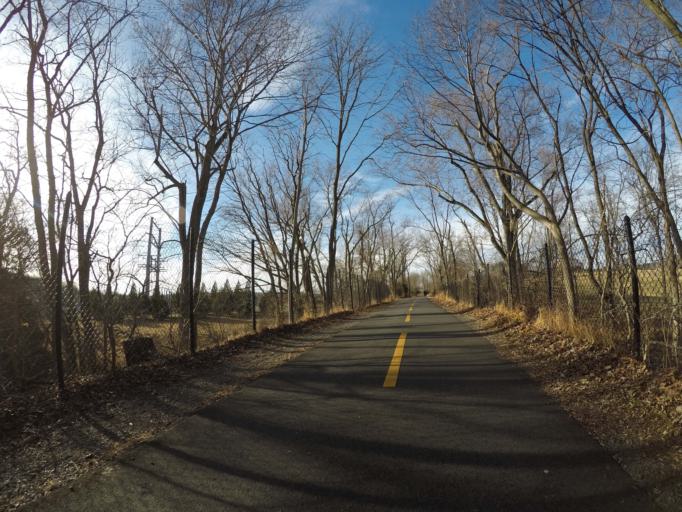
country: US
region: Virginia
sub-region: Loudoun County
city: Leesburg
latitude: 39.1141
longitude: -77.5973
